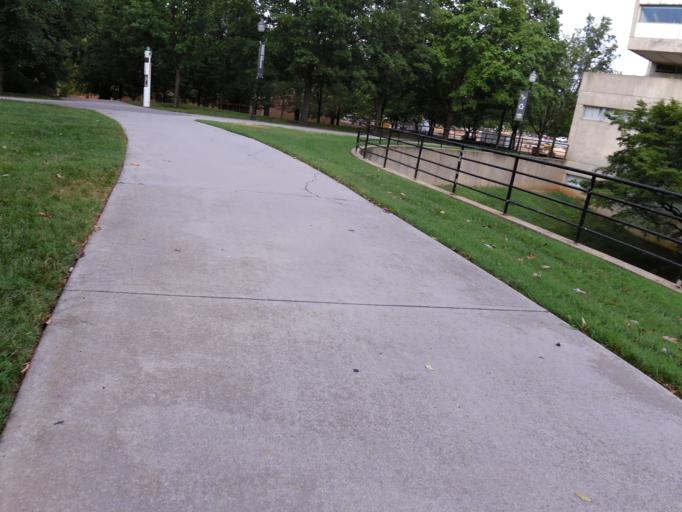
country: US
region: Tennessee
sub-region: Knox County
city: Knoxville
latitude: 35.9531
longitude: -83.9297
